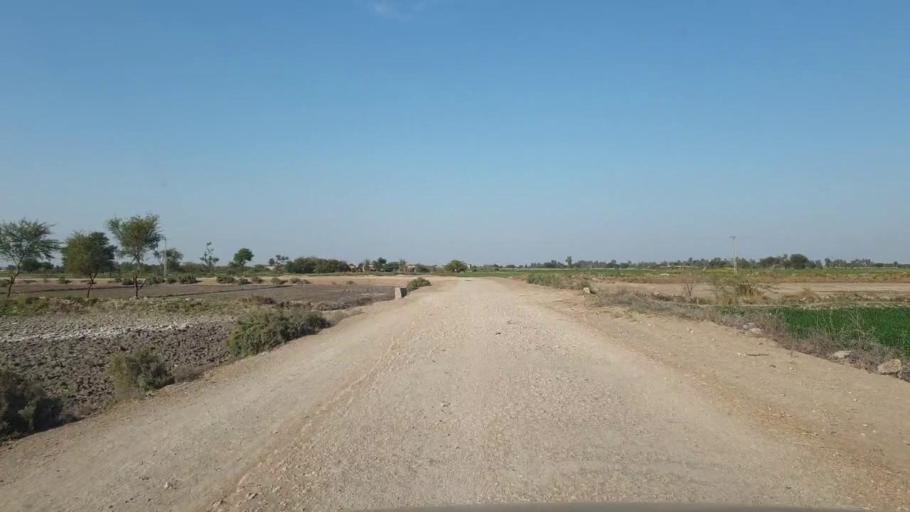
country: PK
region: Sindh
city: Shahpur Chakar
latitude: 26.1682
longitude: 68.6819
